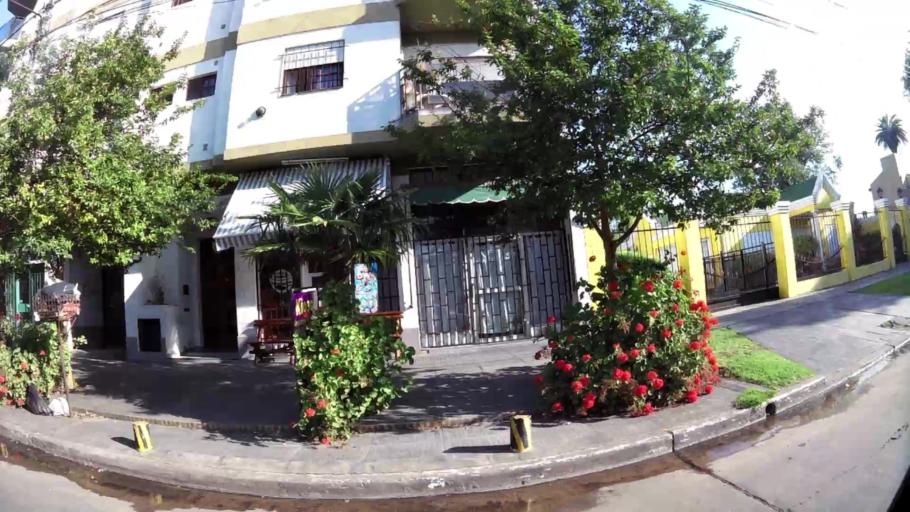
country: AR
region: Buenos Aires
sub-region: Partido de Merlo
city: Merlo
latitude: -34.6702
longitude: -58.7341
